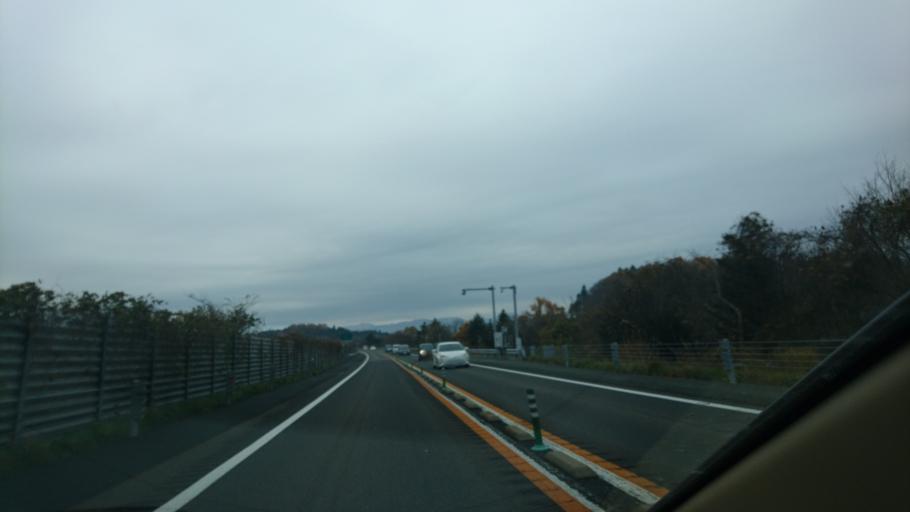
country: JP
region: Iwate
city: Kitakami
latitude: 39.2778
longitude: 141.0462
